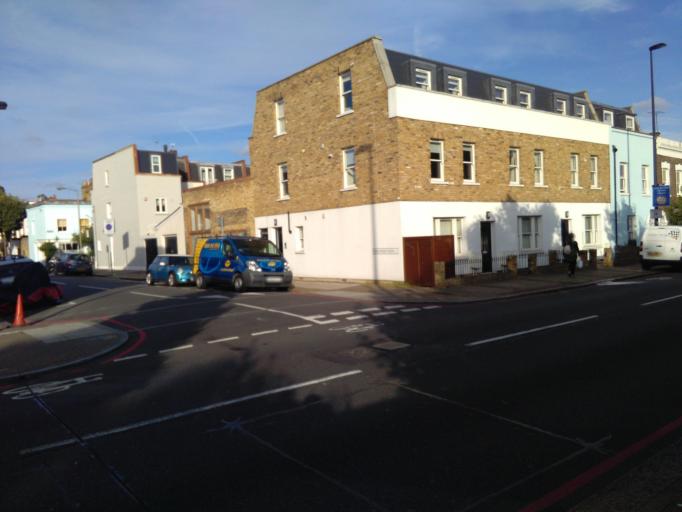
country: GB
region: England
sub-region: Greater London
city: Battersea
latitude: 51.4691
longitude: -0.1637
